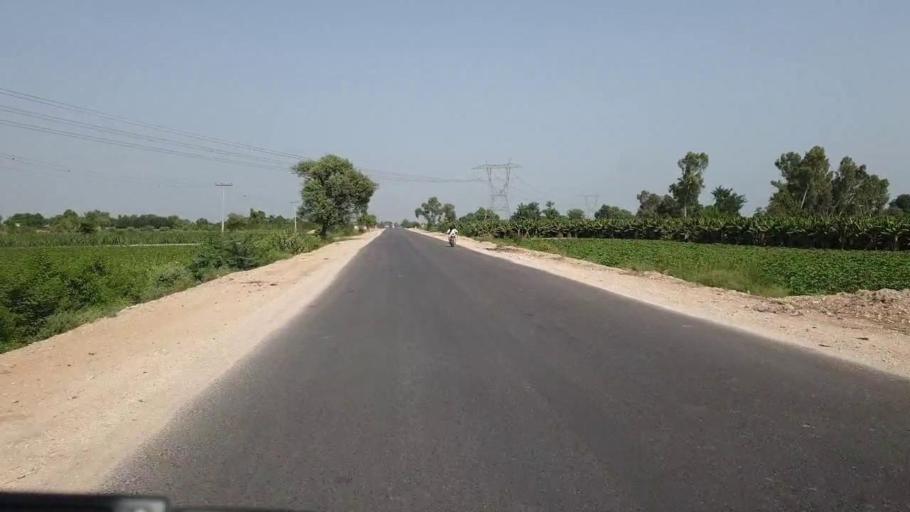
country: PK
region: Sindh
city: Sakrand
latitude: 26.2541
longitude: 68.2002
